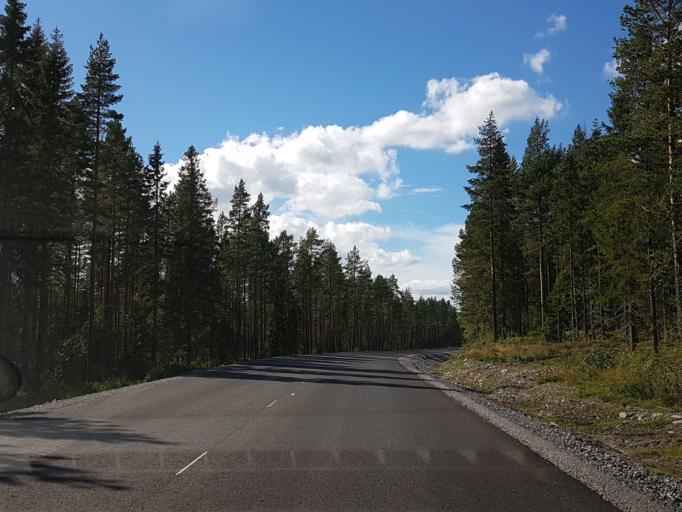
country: SE
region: Vaesterbotten
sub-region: Robertsfors Kommun
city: Robertsfors
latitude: 64.1286
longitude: 20.6509
